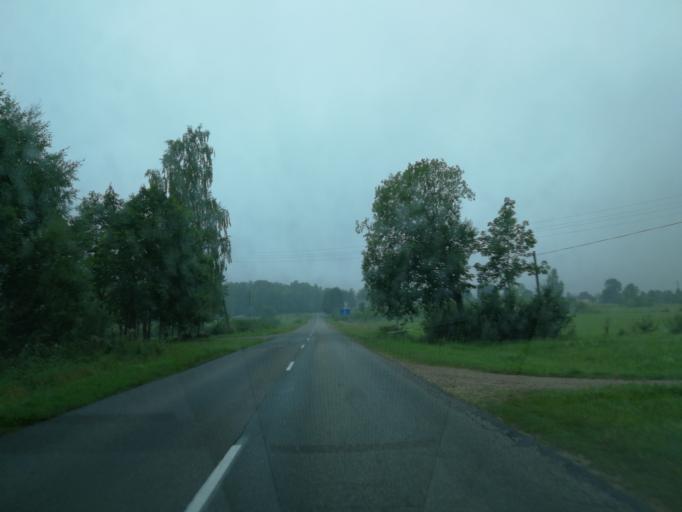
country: LV
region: Preilu Rajons
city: Preili
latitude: 56.2896
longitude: 26.7442
